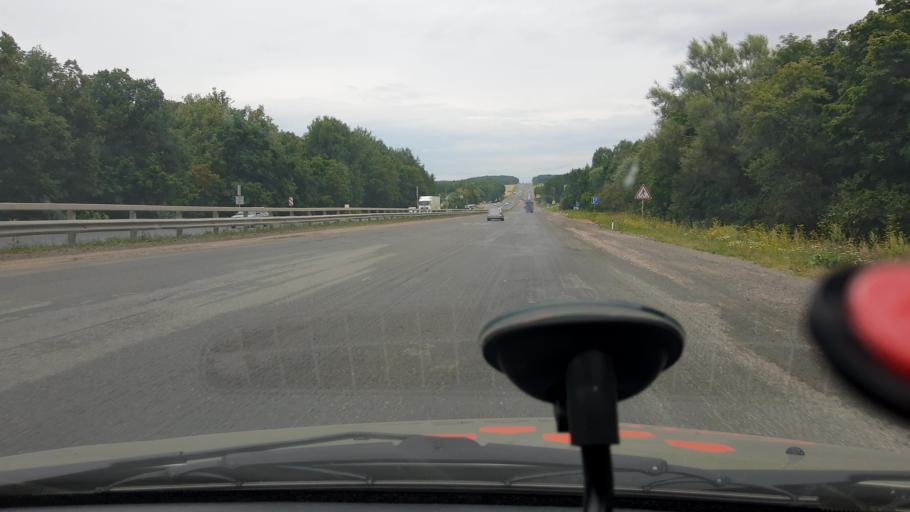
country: RU
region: Bashkortostan
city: Avdon
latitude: 54.6459
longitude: 55.6378
